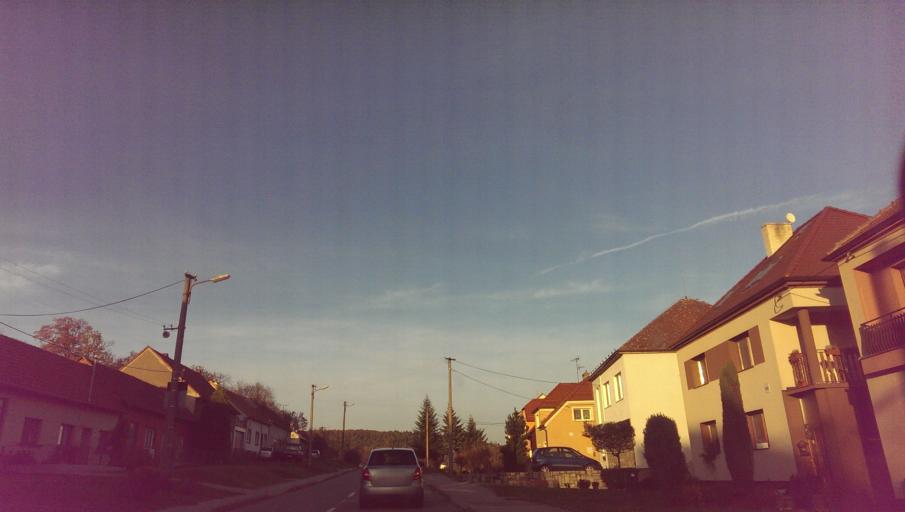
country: CZ
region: Zlin
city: Brezolupy
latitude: 49.1256
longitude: 17.5878
